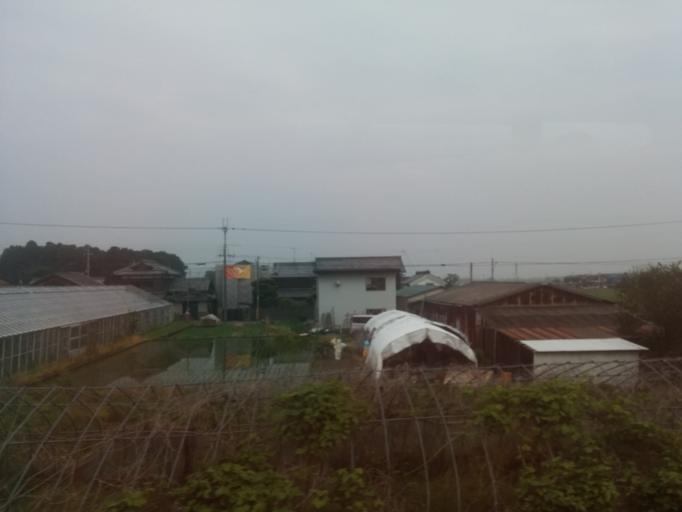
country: JP
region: Shiga Prefecture
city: Omihachiman
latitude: 35.1381
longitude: 136.1259
